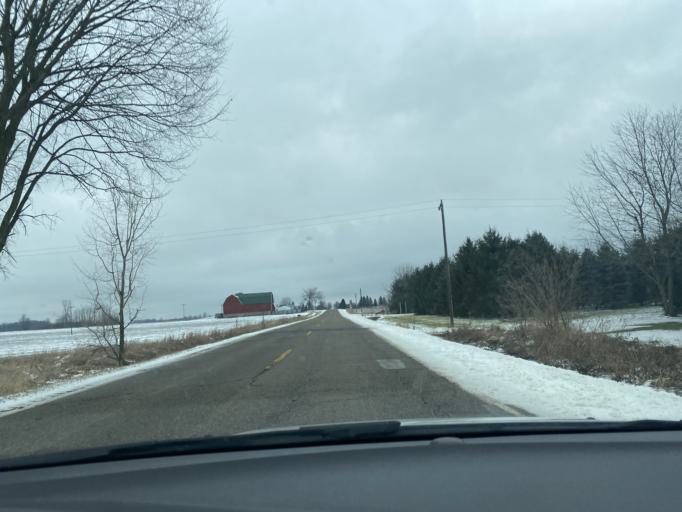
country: US
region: Michigan
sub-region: Lapeer County
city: North Branch
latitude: 43.2101
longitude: -83.1027
